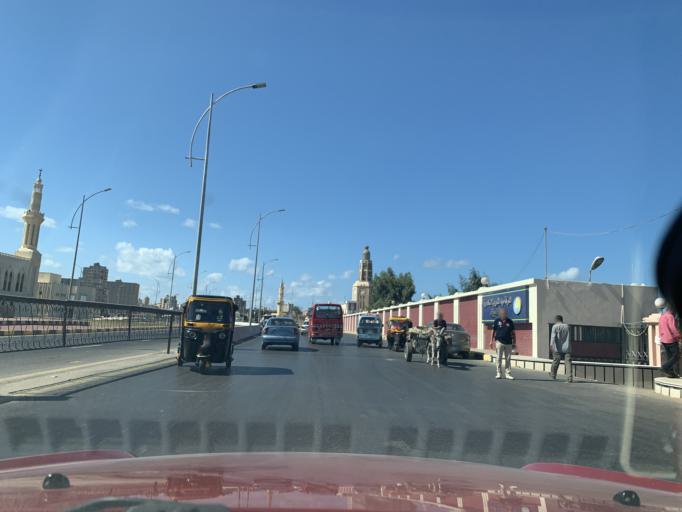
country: EG
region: Alexandria
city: Alexandria
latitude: 31.2220
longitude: 29.9885
